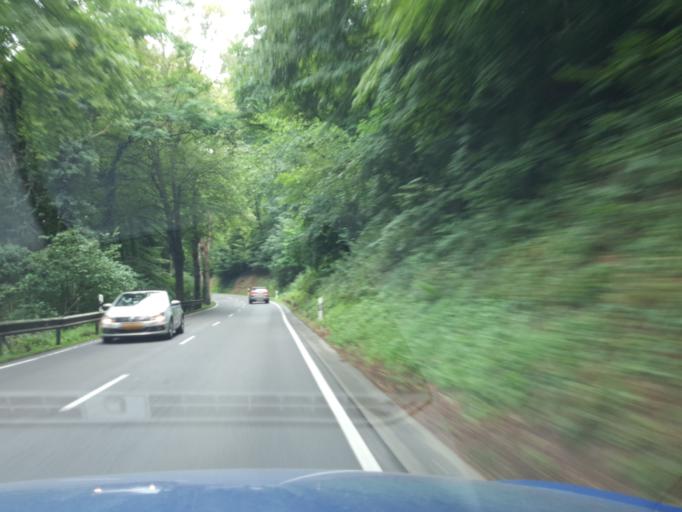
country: LU
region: Luxembourg
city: Rollingen
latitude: 49.7184
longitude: 6.0875
